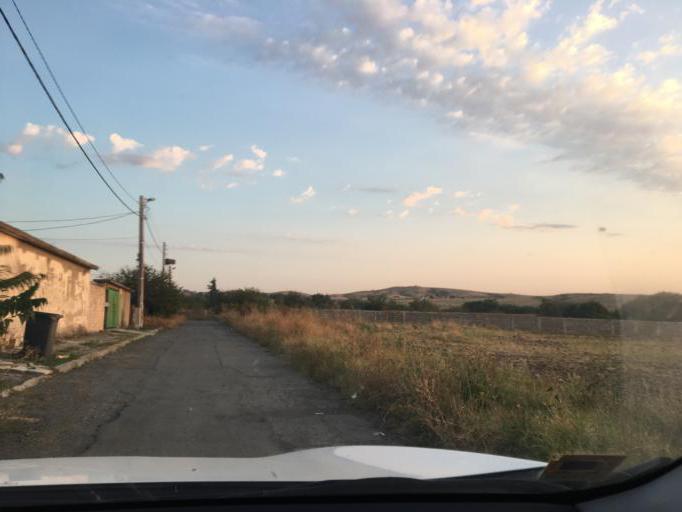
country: BG
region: Burgas
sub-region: Obshtina Burgas
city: Burgas
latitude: 42.6104
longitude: 27.4974
